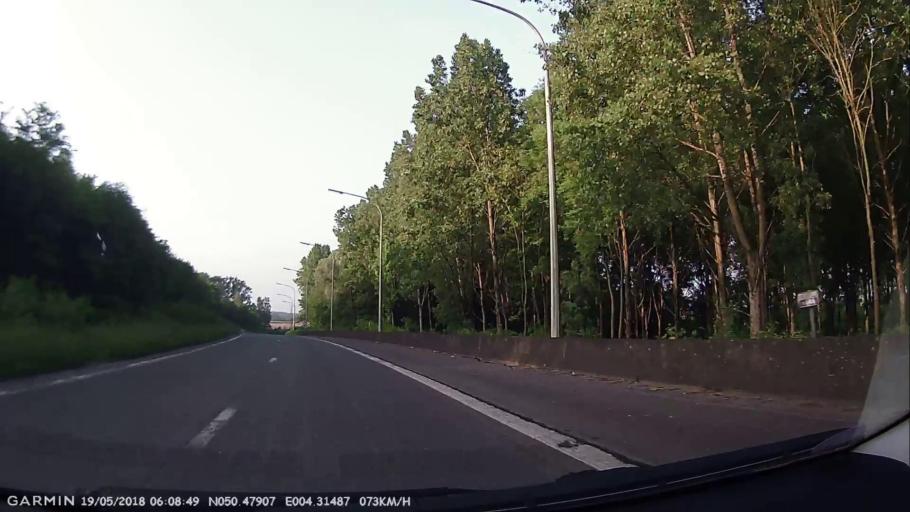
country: BE
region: Wallonia
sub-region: Province du Hainaut
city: Chapelle-lez-Herlaimont
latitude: 50.4789
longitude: 4.3149
